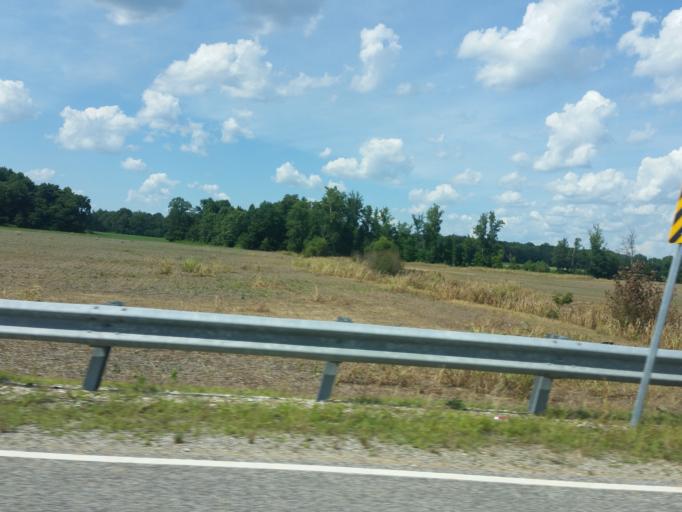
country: US
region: Tennessee
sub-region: Gibson County
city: Milan
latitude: 35.9803
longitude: -88.7663
